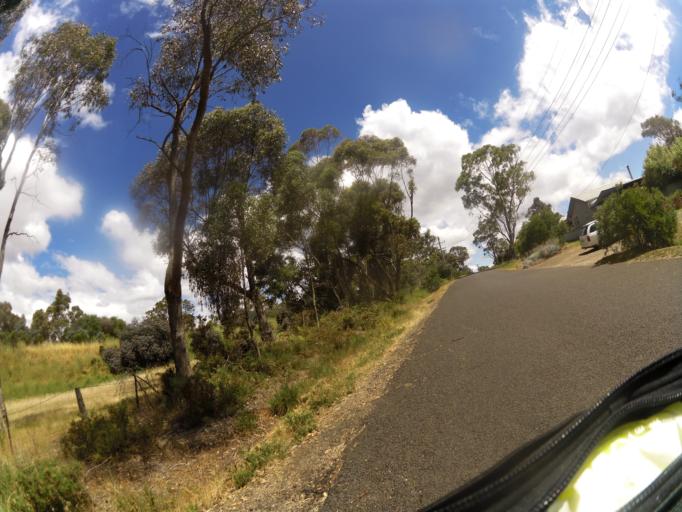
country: AU
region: Victoria
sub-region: Mount Alexander
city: Castlemaine
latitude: -37.0025
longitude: 144.2536
